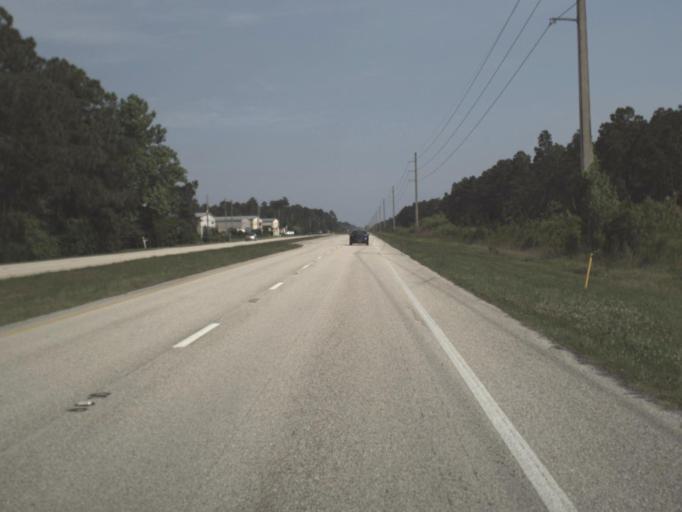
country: US
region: Florida
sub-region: Saint Johns County
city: Villano Beach
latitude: 30.0037
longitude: -81.3843
